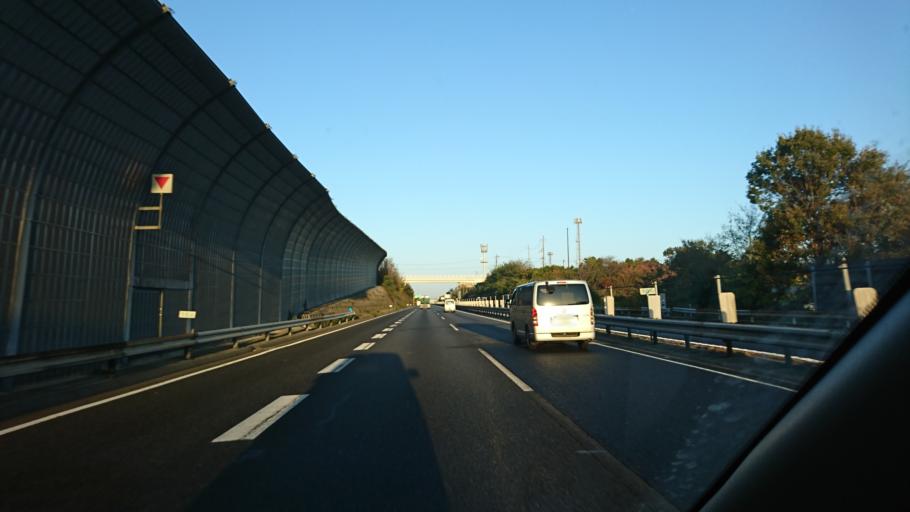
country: JP
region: Hyogo
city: Akashi
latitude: 34.7053
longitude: 134.9537
